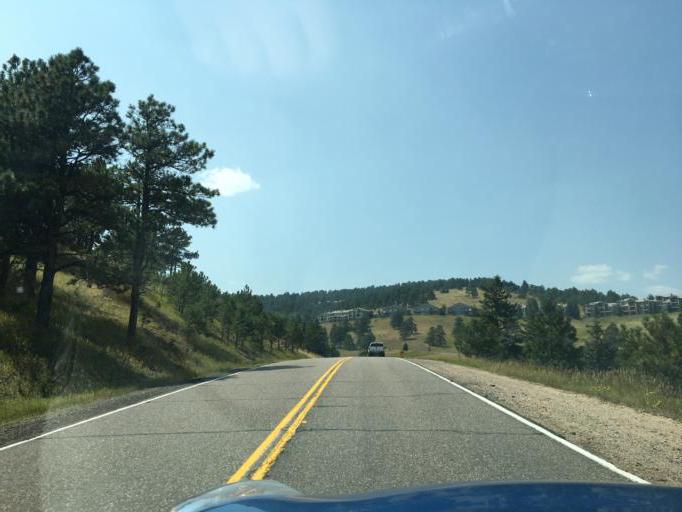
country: US
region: Colorado
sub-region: Jefferson County
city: Genesee
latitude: 39.7041
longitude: -105.2772
